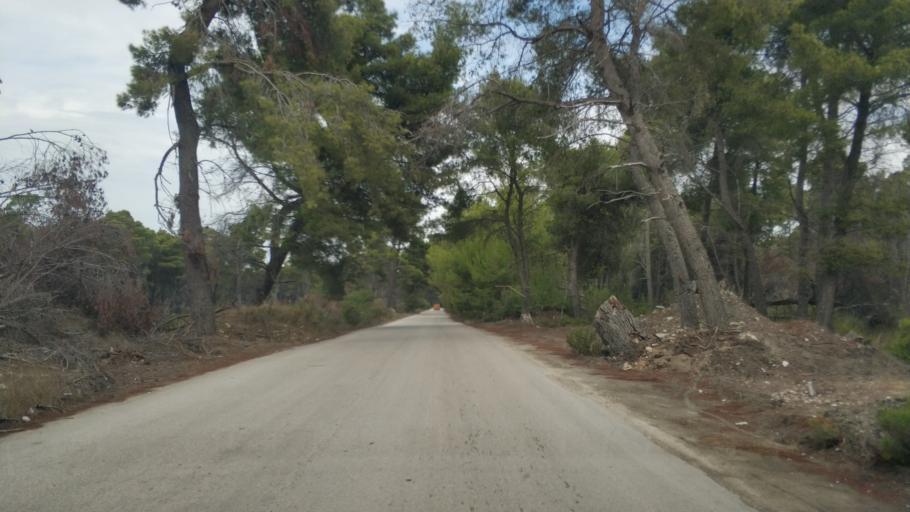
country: AL
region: Vlore
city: Vlore
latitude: 40.4792
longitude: 19.4509
